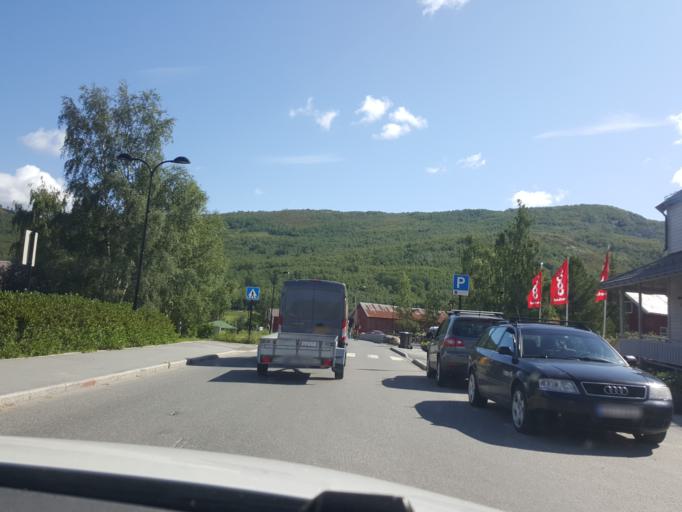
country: NO
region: Nordland
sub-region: Bodo
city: Loding
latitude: 67.1162
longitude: 15.0056
